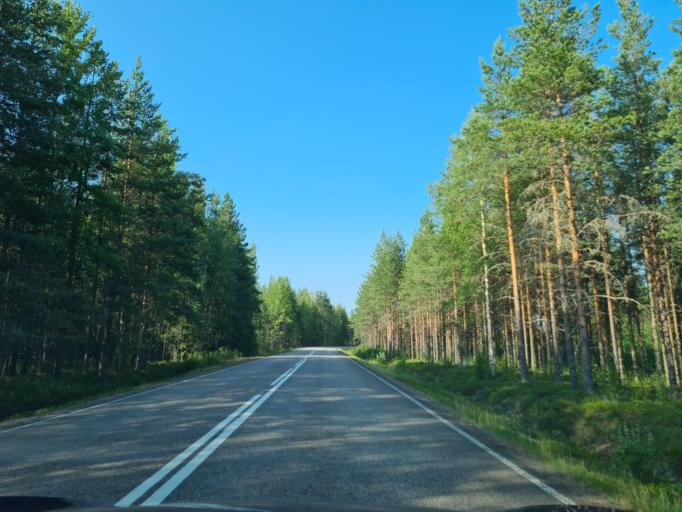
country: FI
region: Satakunta
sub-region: Pohjois-Satakunta
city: Karvia
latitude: 62.3139
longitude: 22.6569
